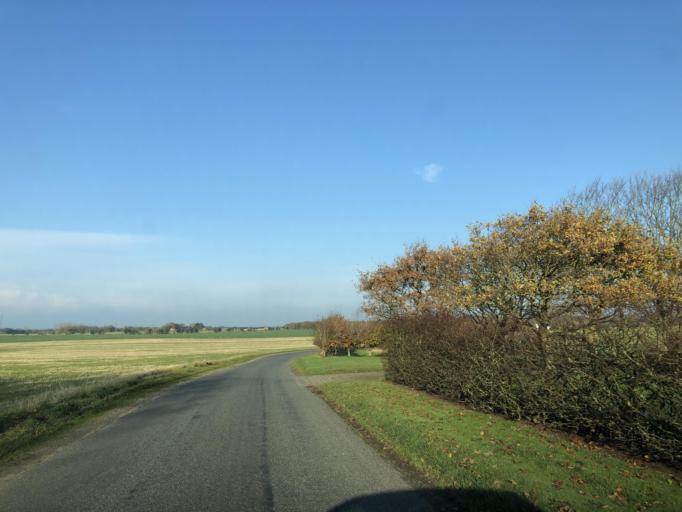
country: DK
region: Central Jutland
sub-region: Holstebro Kommune
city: Vinderup
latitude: 56.3980
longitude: 8.7465
